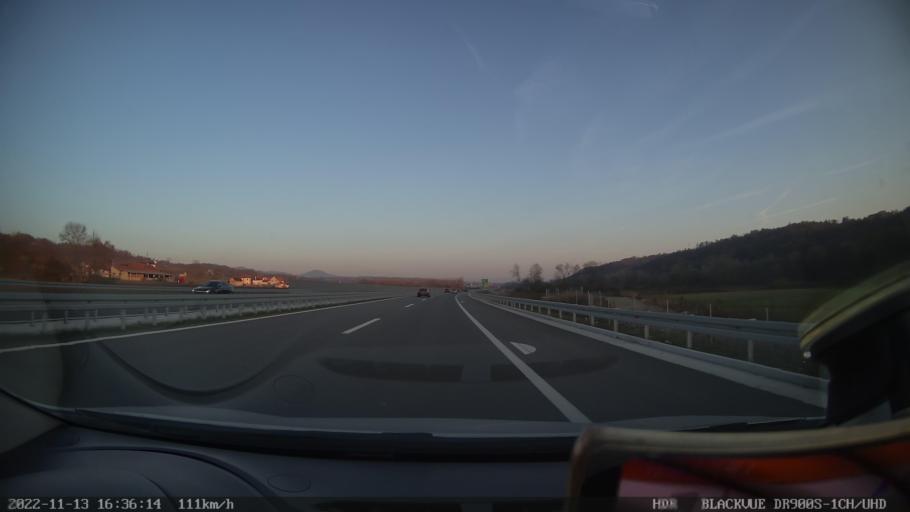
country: RS
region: Central Serbia
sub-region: Moravicki Okrug
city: Cacak
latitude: 43.9230
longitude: 20.3734
